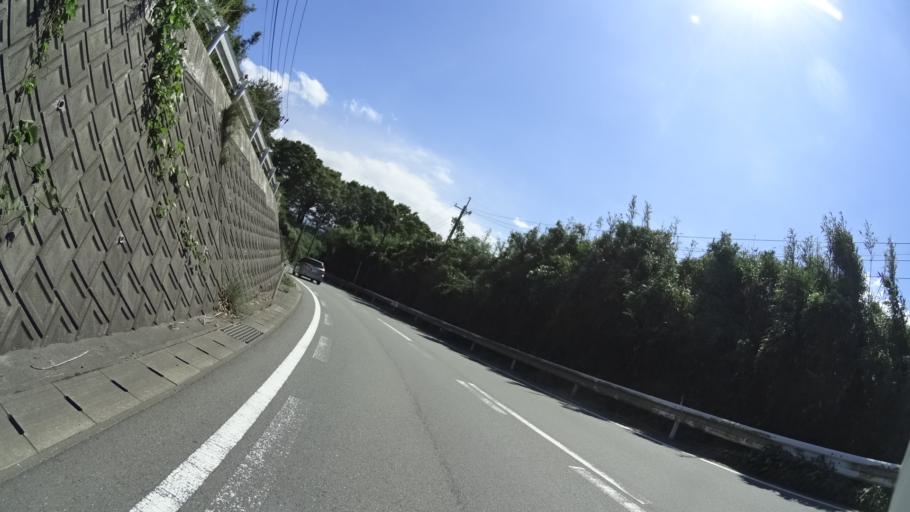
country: JP
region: Kumamoto
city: Aso
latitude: 32.8897
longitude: 130.9920
